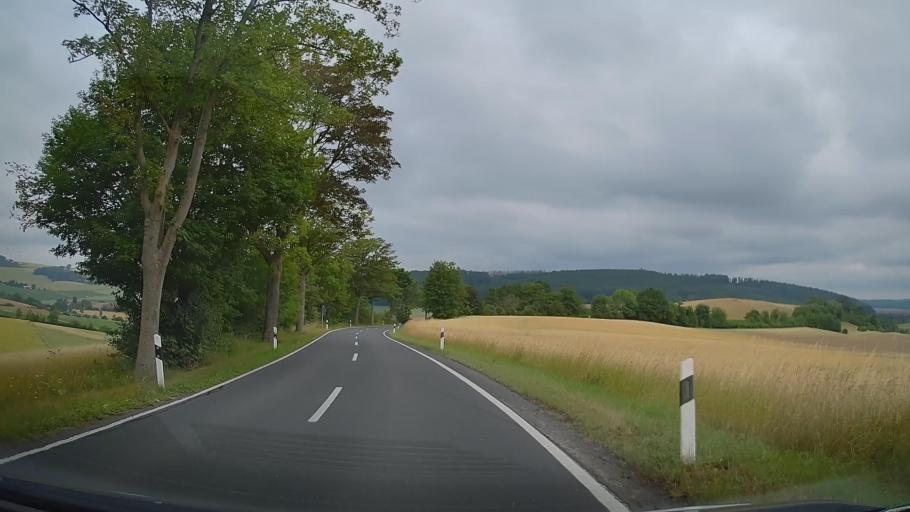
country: DE
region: Lower Saxony
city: Bad Pyrmont
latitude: 52.0048
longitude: 9.2077
